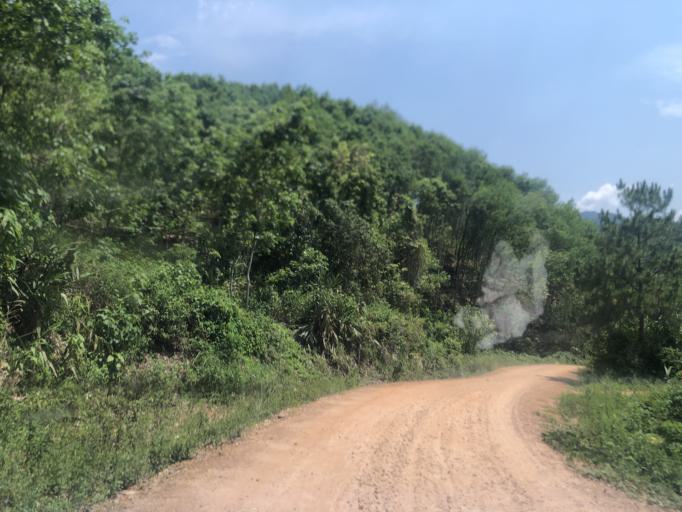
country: LA
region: Phongsali
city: Phongsali
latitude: 21.4155
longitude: 101.9697
